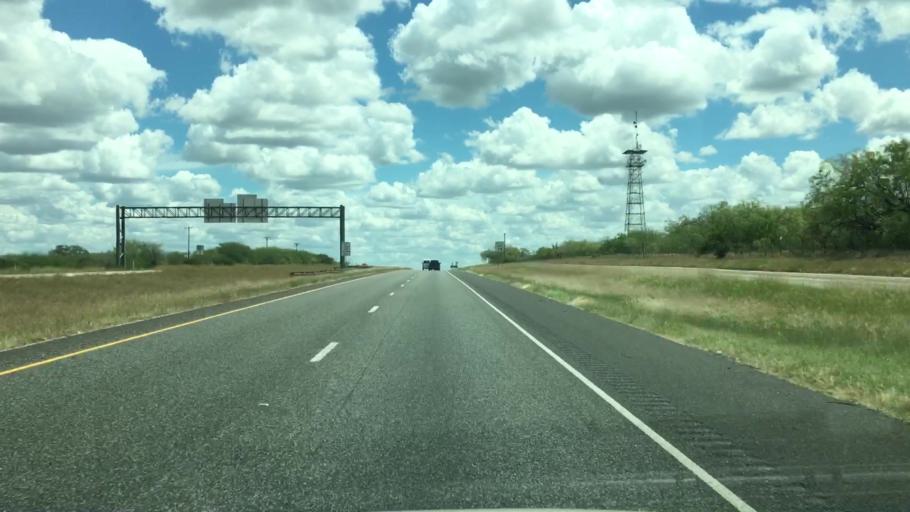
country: US
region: Texas
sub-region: Atascosa County
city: Pleasanton
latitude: 28.9024
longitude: -98.4243
